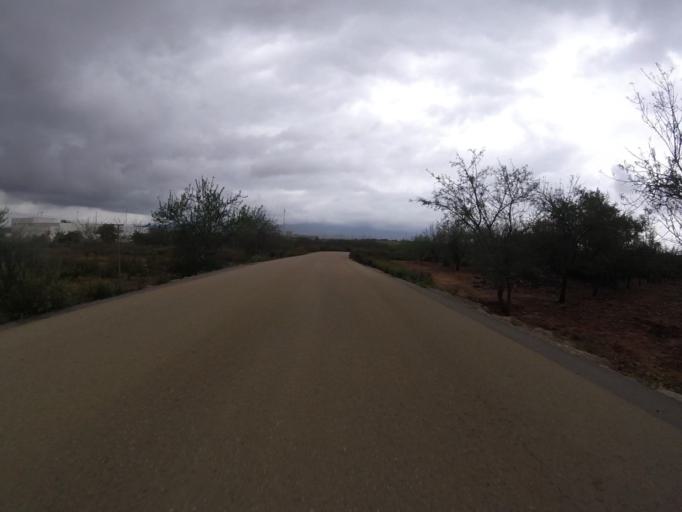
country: ES
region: Valencia
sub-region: Provincia de Castello
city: Benlloch
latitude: 40.2051
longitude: 0.0716
